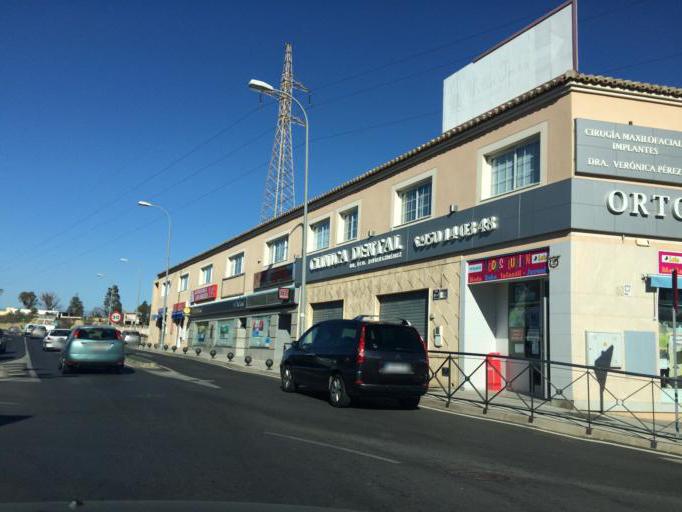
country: ES
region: Andalusia
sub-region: Provincia de Almeria
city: Huercal de Almeria
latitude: 36.8700
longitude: -2.4393
